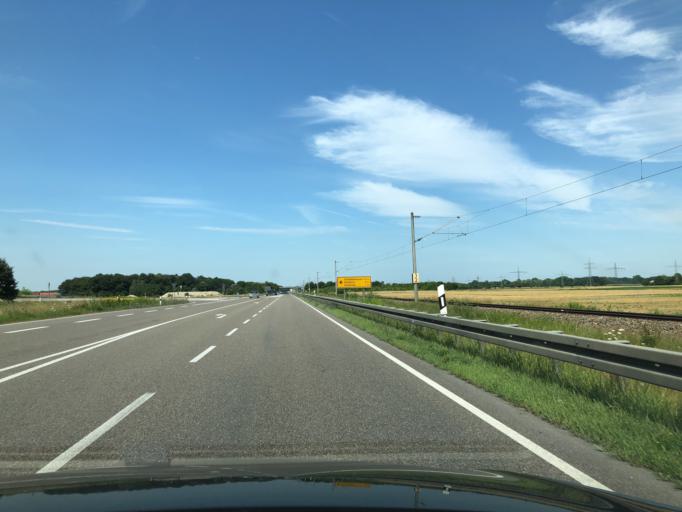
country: DE
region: Bavaria
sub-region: Upper Bavaria
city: Karlskron
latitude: 48.7038
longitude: 11.4048
